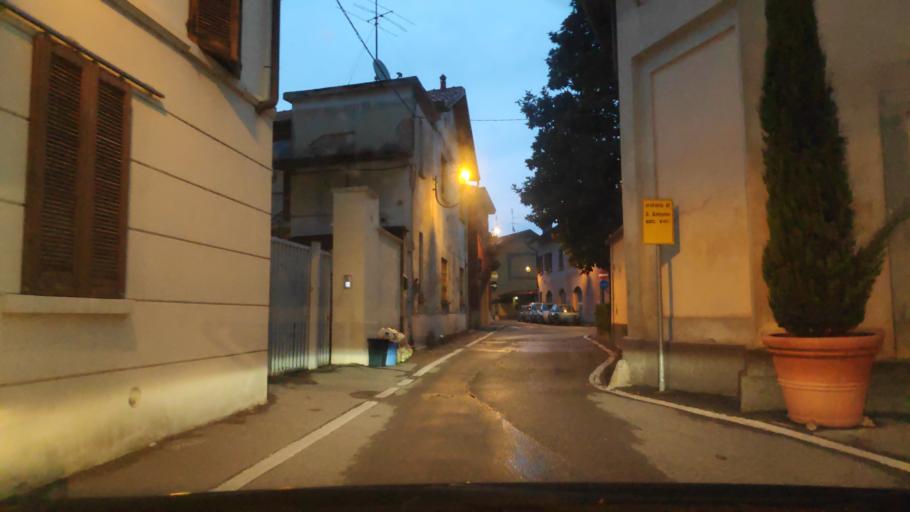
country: IT
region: Lombardy
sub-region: Citta metropolitana di Milano
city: Melzo
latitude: 45.4972
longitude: 9.4250
